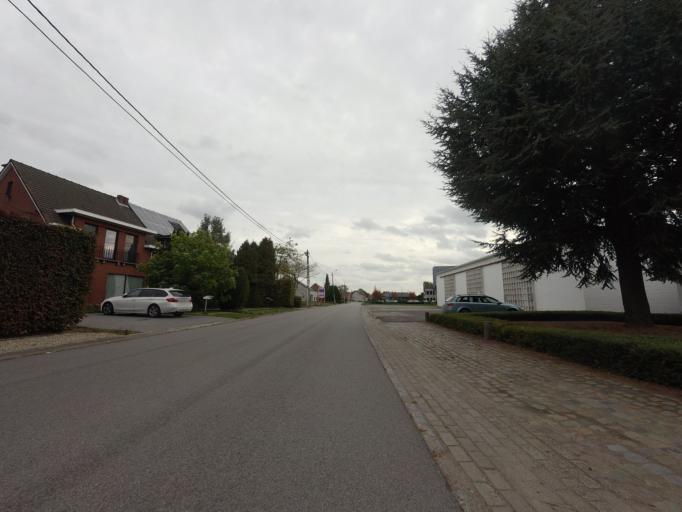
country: BE
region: Flanders
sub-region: Provincie Antwerpen
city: Rumst
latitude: 51.0483
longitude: 4.4133
